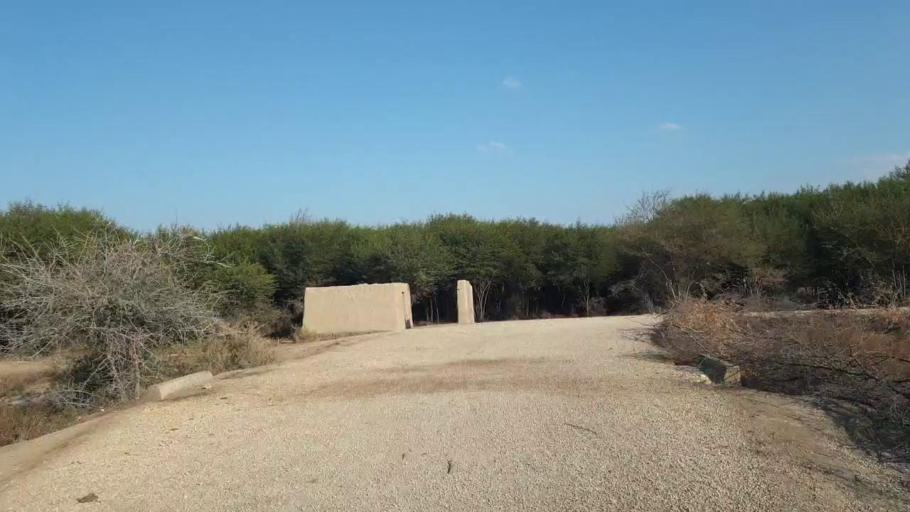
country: PK
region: Sindh
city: Shahpur Chakar
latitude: 26.1189
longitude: 68.5768
